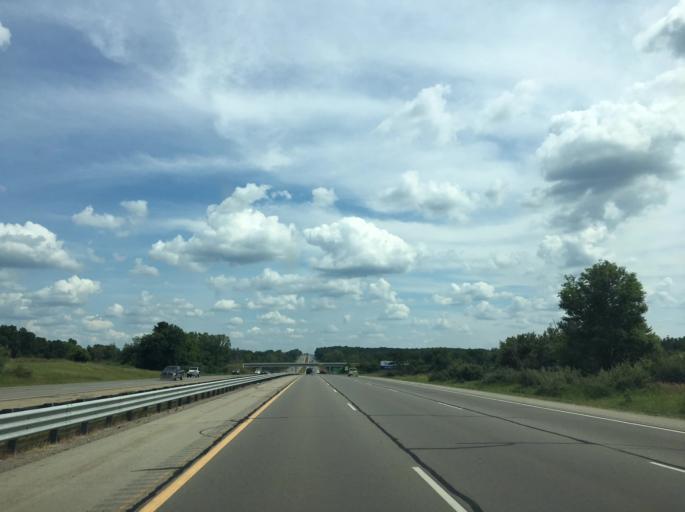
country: US
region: Michigan
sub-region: Oakland County
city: Holly
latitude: 42.8470
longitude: -83.5872
